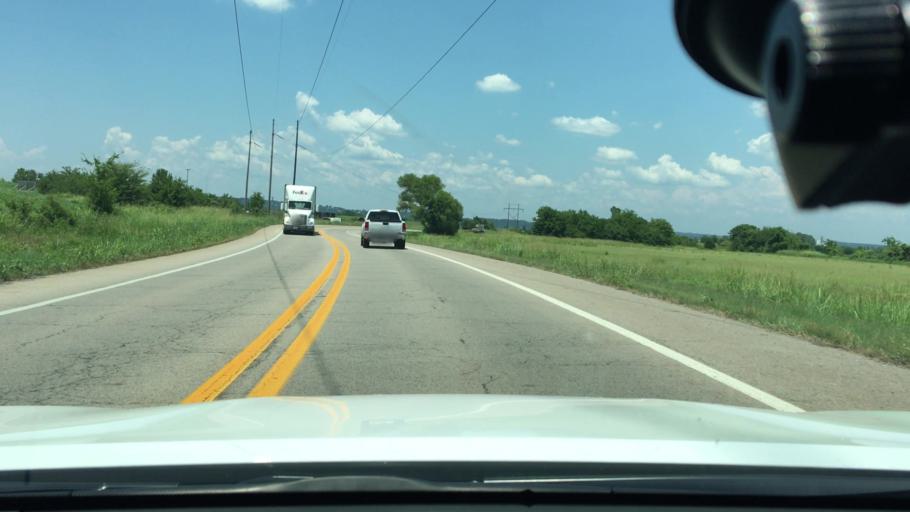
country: US
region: Arkansas
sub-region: Crawford County
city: Van Buren
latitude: 35.3908
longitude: -94.3297
